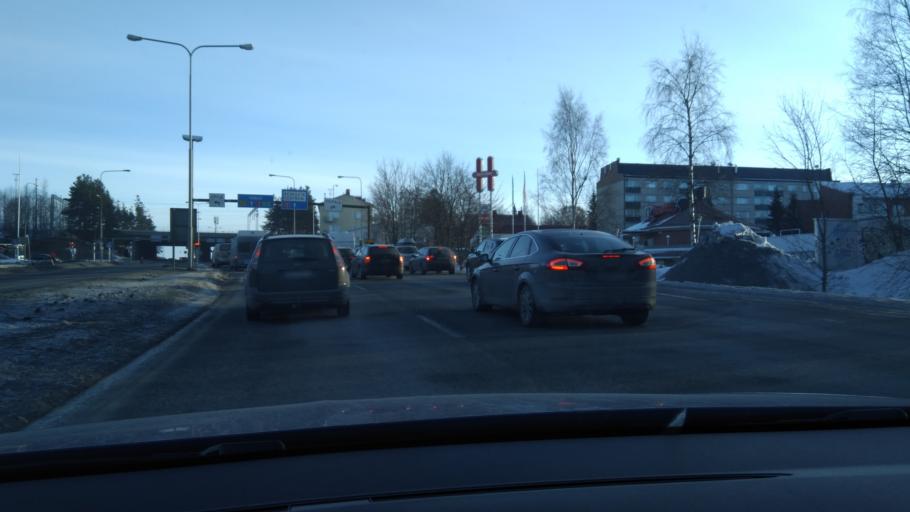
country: FI
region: Pirkanmaa
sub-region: Tampere
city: Pirkkala
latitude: 61.5072
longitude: 23.6872
